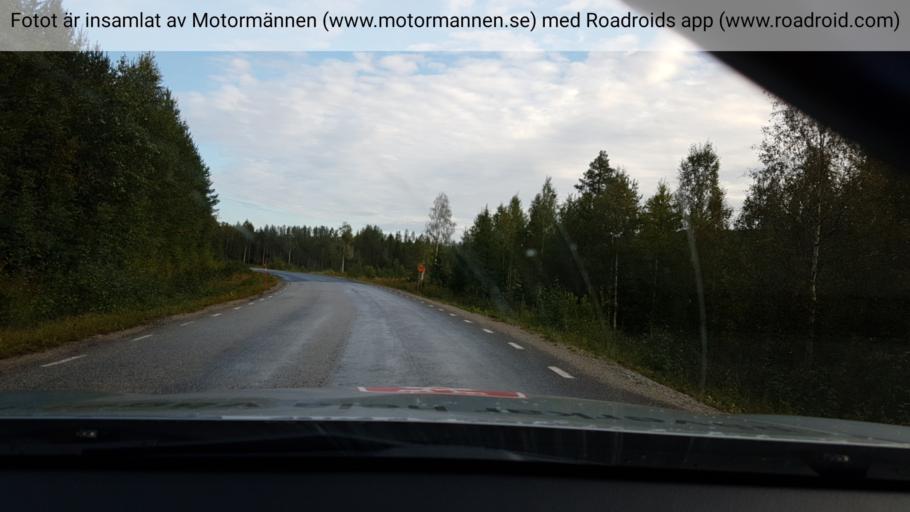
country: SE
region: Vaesterbotten
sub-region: Vindelns Kommun
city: Vindeln
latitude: 64.2081
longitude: 19.7635
